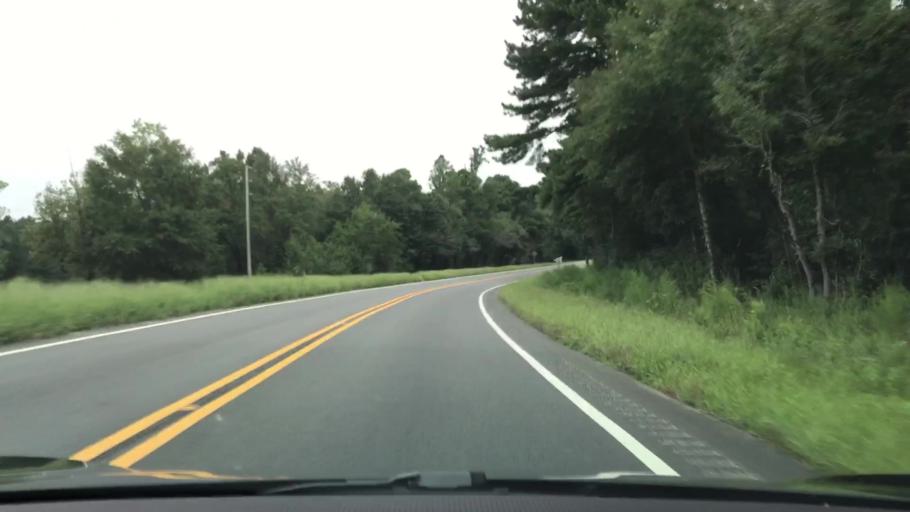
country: US
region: Alabama
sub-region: Covington County
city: Opp
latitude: 31.2270
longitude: -86.1617
